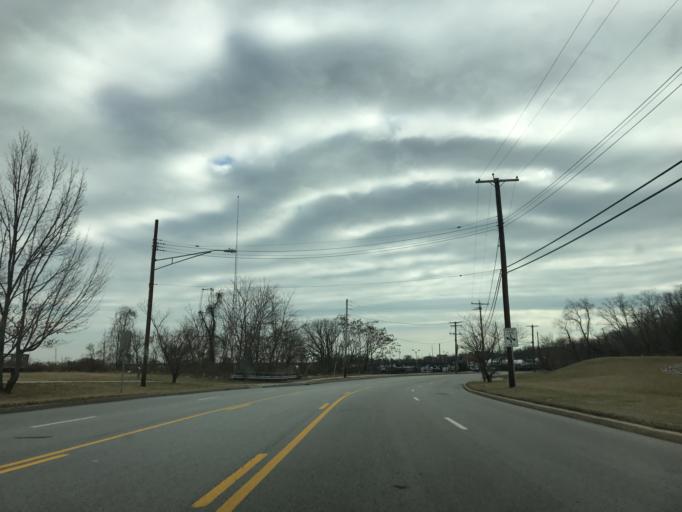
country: US
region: Maryland
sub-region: Baltimore County
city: Baltimore Highlands
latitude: 39.2569
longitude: -76.6285
